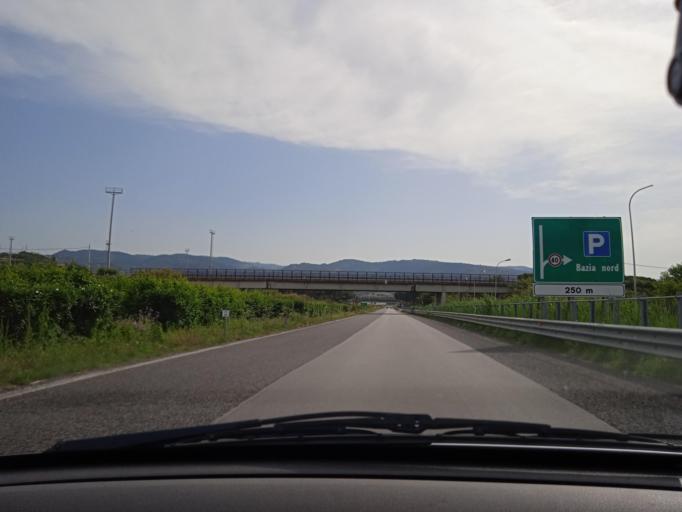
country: IT
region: Sicily
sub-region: Messina
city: Tonnarella
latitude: 38.1222
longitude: 15.1183
